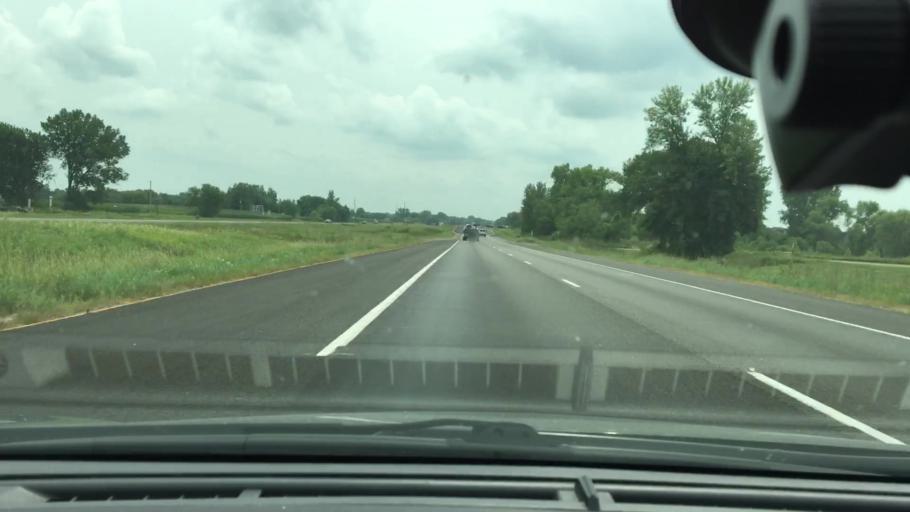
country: US
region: Minnesota
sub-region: Mille Lacs County
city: Princeton
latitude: 45.6092
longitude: -93.6074
